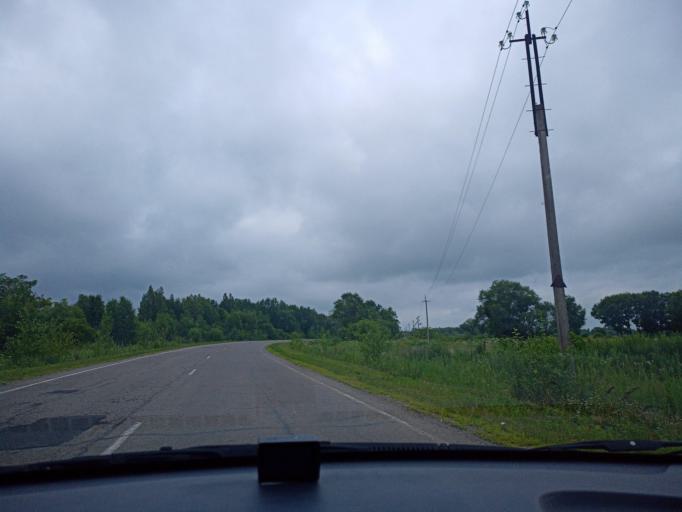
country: RU
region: Primorskiy
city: Novopokrovka
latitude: 45.8890
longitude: 134.8473
